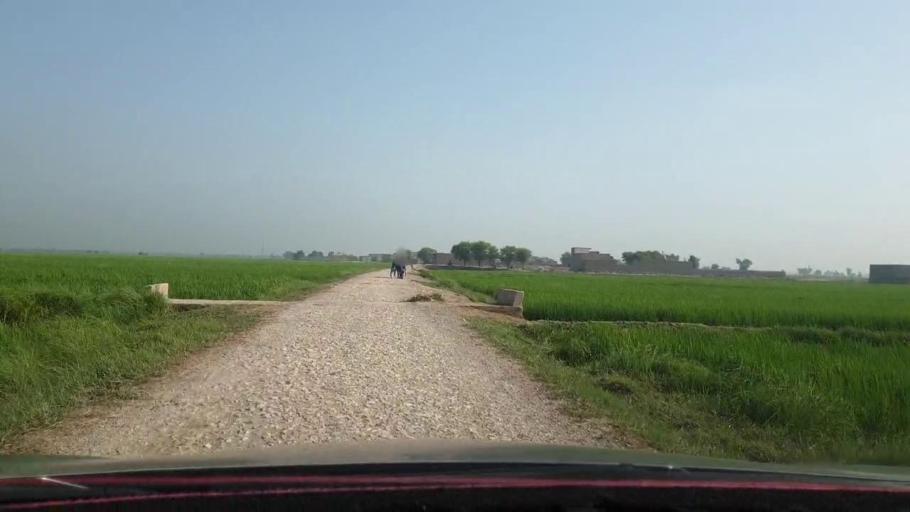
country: PK
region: Sindh
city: Nasirabad
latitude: 27.4724
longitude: 67.9234
